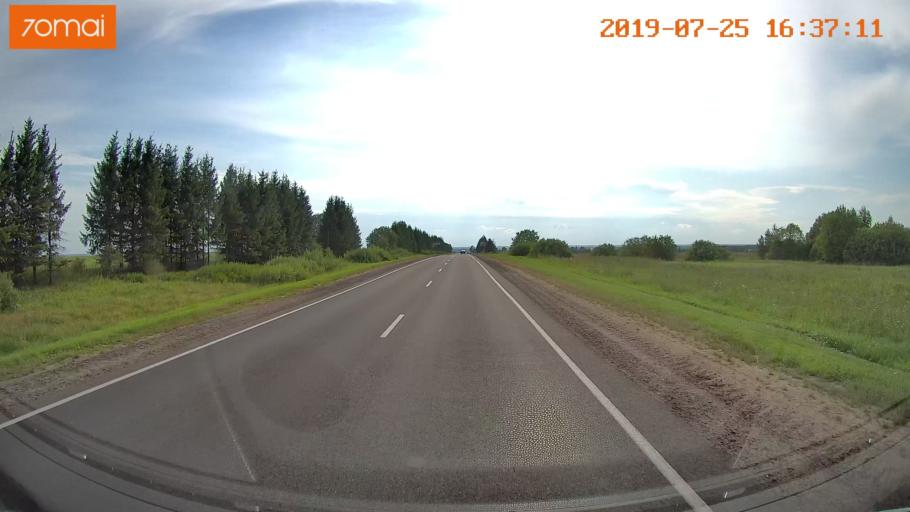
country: RU
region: Ivanovo
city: Privolzhsk
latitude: 57.3913
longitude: 41.3830
